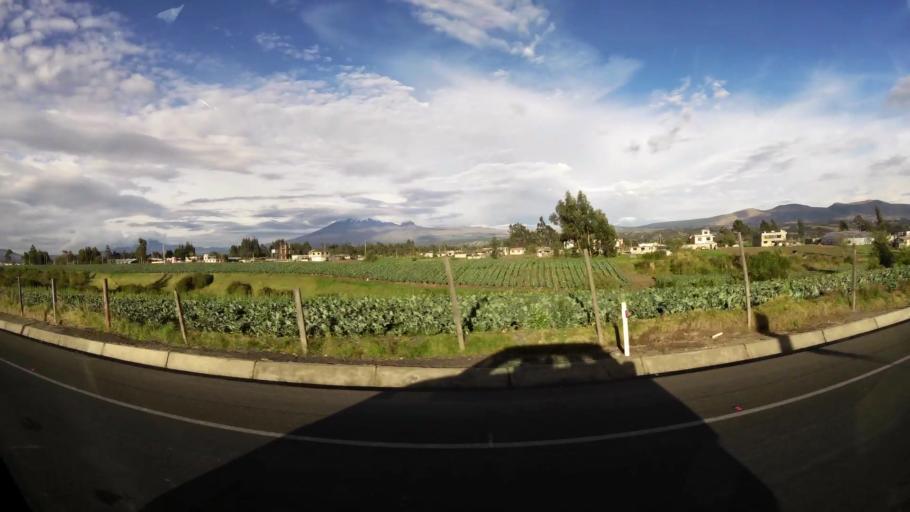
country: EC
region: Cotopaxi
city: Saquisili
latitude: -0.8184
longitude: -78.6243
